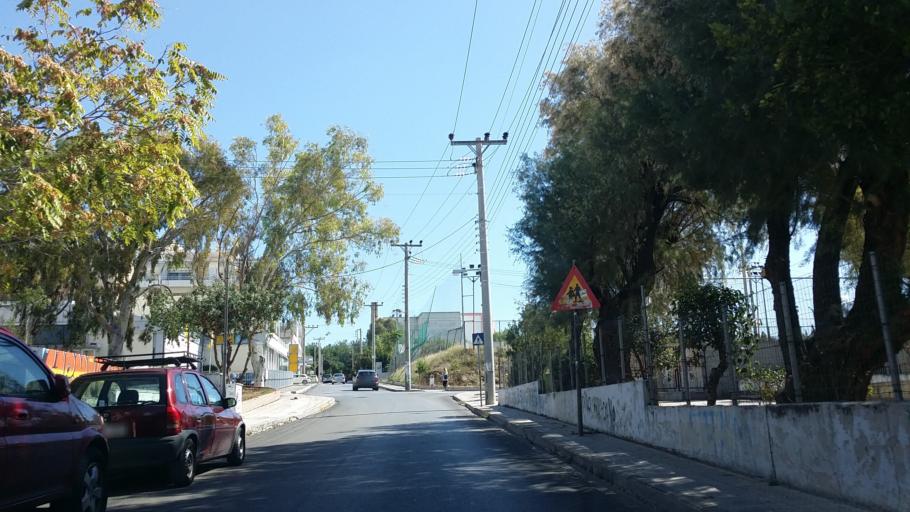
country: GR
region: Attica
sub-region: Nomarchia Athinas
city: Nea Filadelfeia
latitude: 38.0488
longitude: 23.7440
